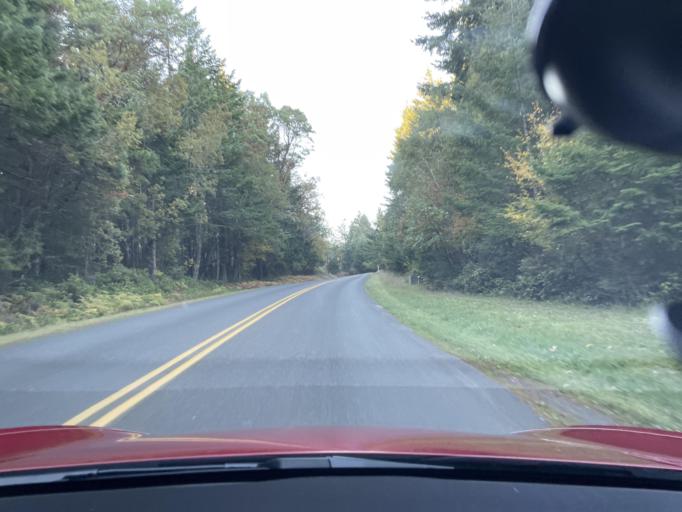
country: US
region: Washington
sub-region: San Juan County
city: Friday Harbor
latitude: 48.5568
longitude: -123.1646
